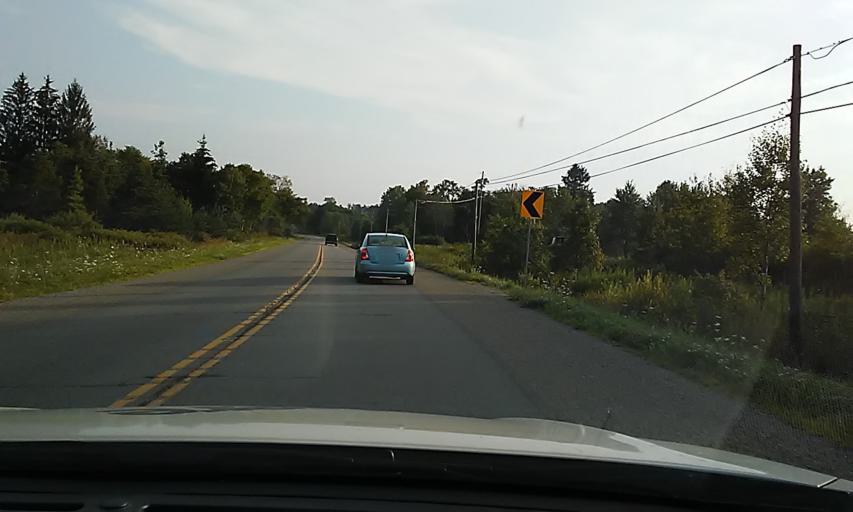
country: US
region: Pennsylvania
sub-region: McKean County
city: Kane
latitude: 41.6968
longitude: -78.7167
